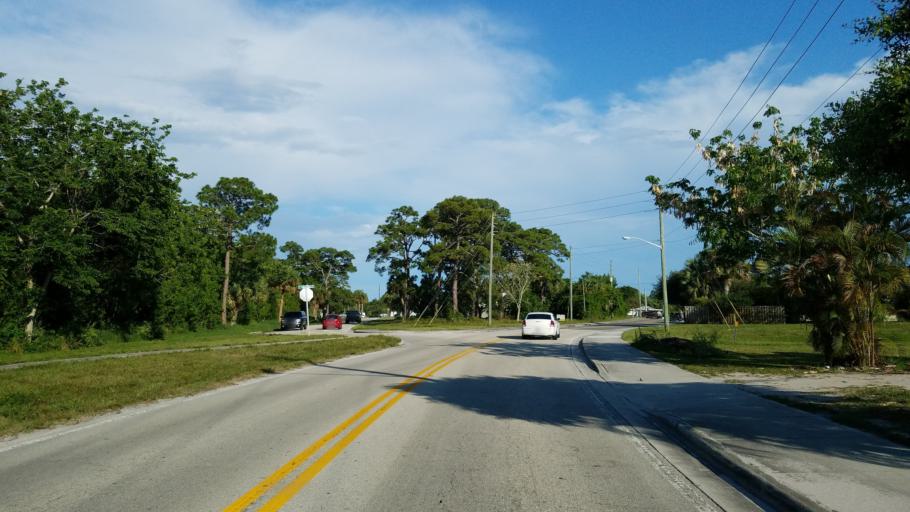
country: US
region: Florida
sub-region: Martin County
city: Port Salerno
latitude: 27.1476
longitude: -80.2009
